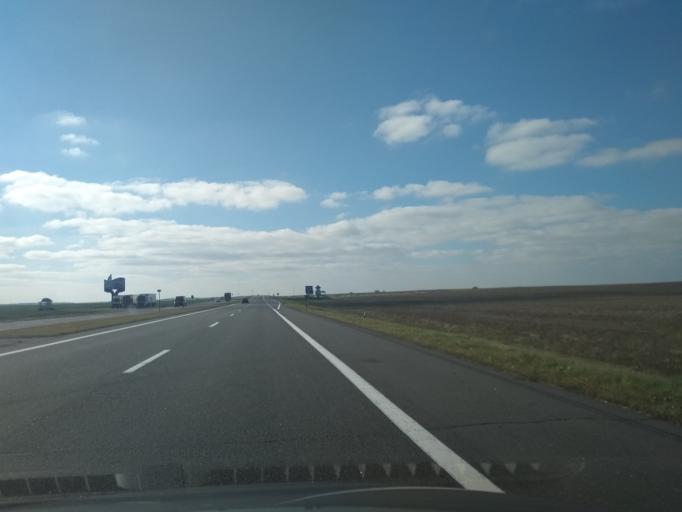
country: BY
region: Minsk
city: Snow
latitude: 53.2780
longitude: 26.3137
